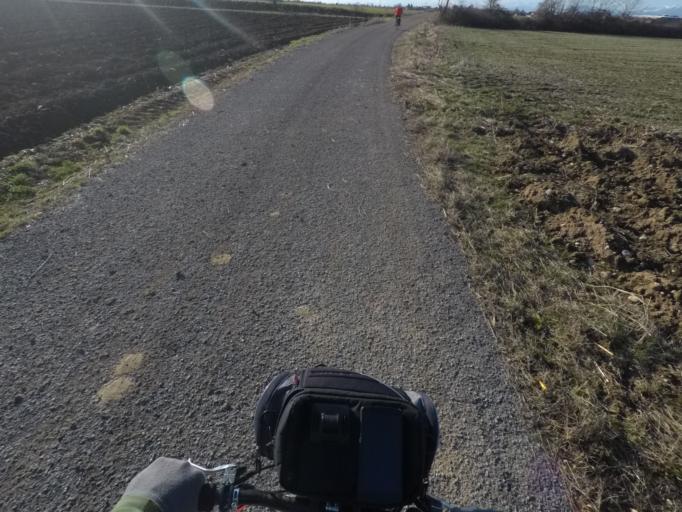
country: IT
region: Friuli Venezia Giulia
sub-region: Provincia di Udine
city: Remanzacco
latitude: 46.0997
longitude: 13.3215
